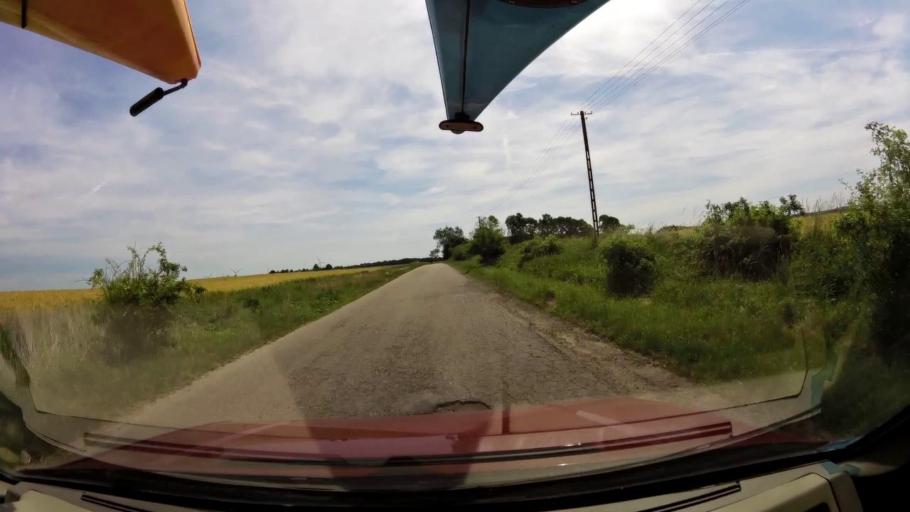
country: PL
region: West Pomeranian Voivodeship
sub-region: Powiat slawienski
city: Darlowo
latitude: 54.3152
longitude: 16.4198
